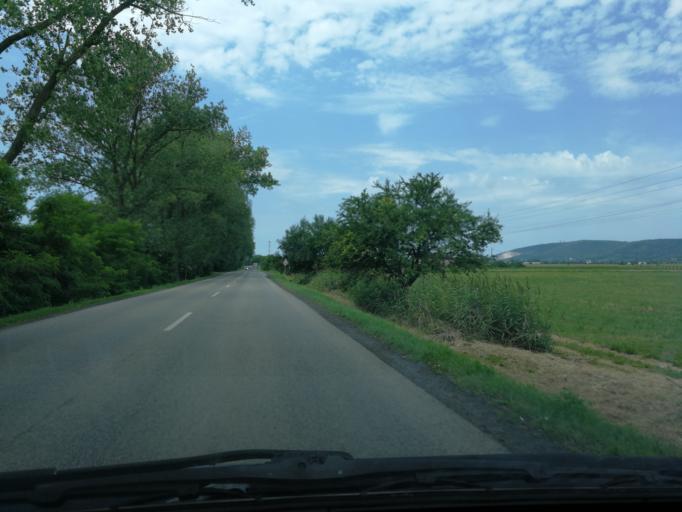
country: HU
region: Baranya
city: Siklos
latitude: 45.8512
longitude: 18.3277
